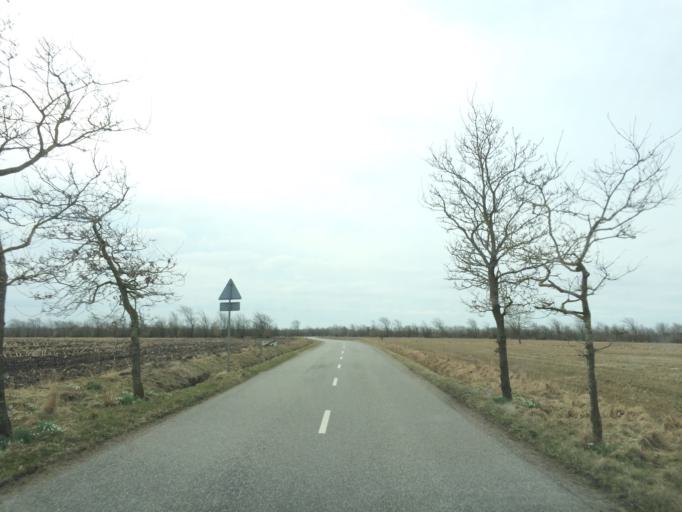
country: DK
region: Central Jutland
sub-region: Ringkobing-Skjern Kommune
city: Tarm
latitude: 55.8204
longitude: 8.4051
